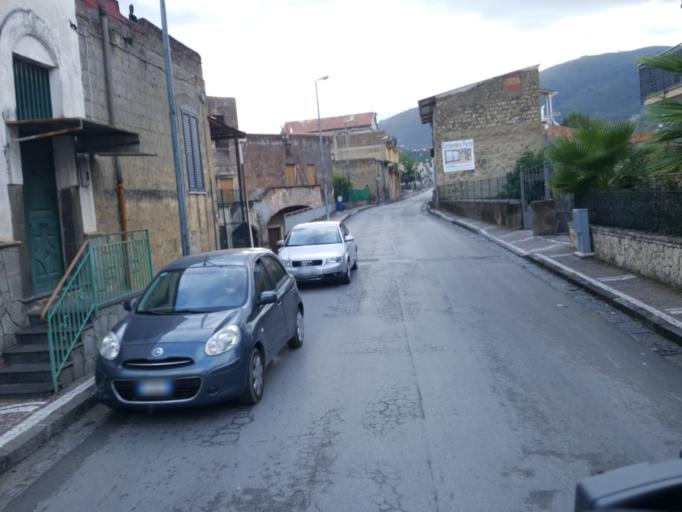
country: IT
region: Campania
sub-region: Provincia di Napoli
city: Palma Campania
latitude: 40.8797
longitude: 14.5526
